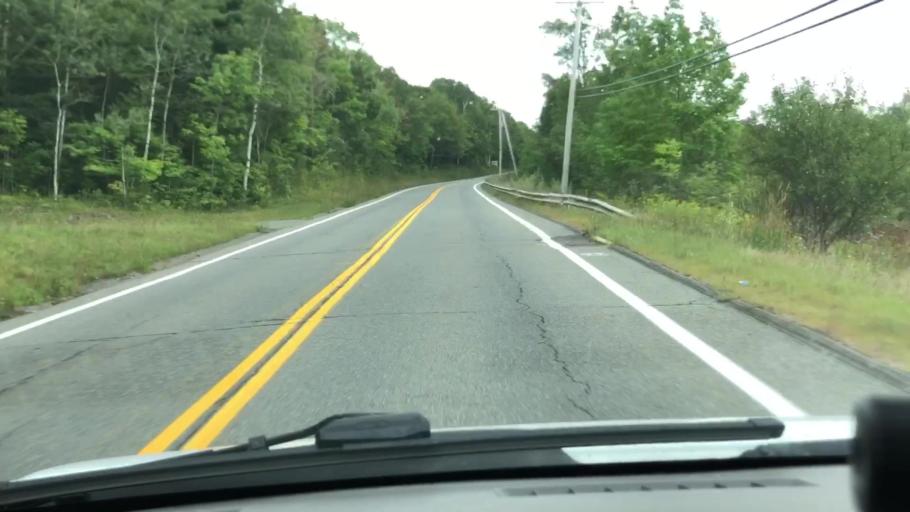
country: US
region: Massachusetts
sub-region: Berkshire County
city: North Adams
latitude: 42.6926
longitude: -73.0263
